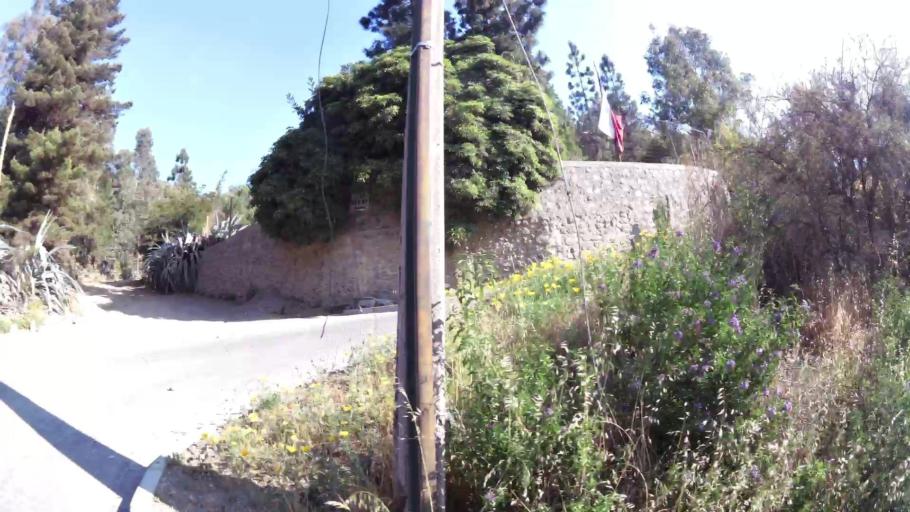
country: CL
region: Santiago Metropolitan
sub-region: Provincia de Santiago
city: Villa Presidente Frei, Nunoa, Santiago, Chile
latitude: -33.3648
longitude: -70.4879
